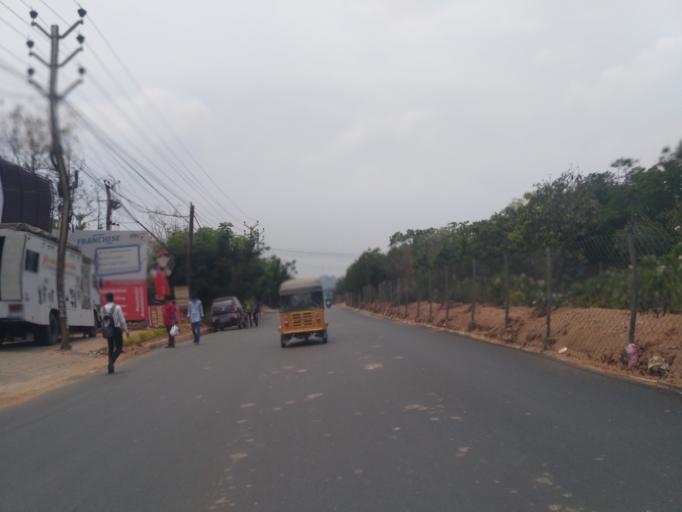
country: IN
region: Telangana
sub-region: Rangareddi
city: Kukatpalli
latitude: 17.4523
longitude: 78.3866
